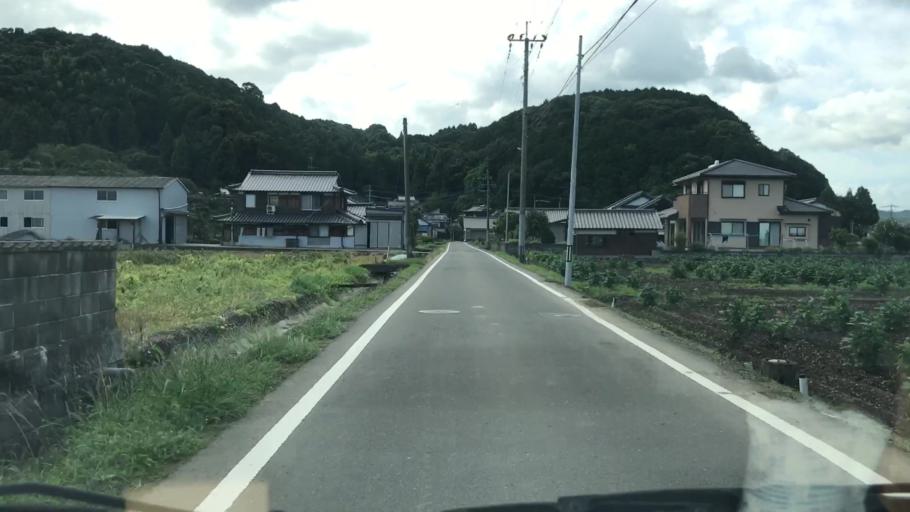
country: JP
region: Saga Prefecture
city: Kashima
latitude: 33.1172
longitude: 130.0722
